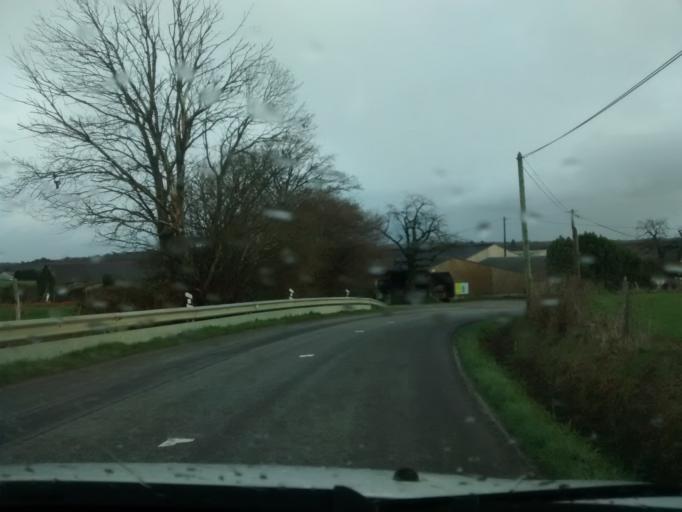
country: FR
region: Brittany
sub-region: Departement d'Ille-et-Vilaine
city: Liffre
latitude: 48.1870
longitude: -1.5046
